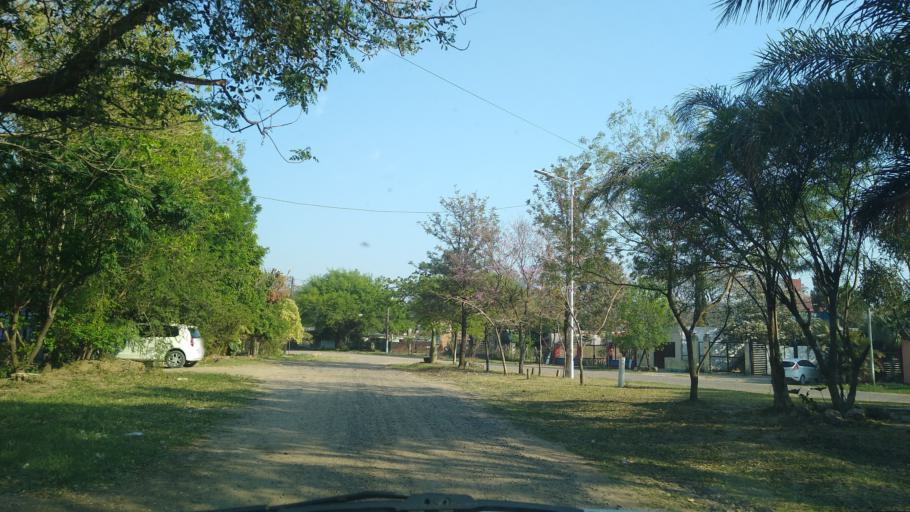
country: AR
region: Chaco
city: Barranqueras
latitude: -27.4749
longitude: -58.9527
